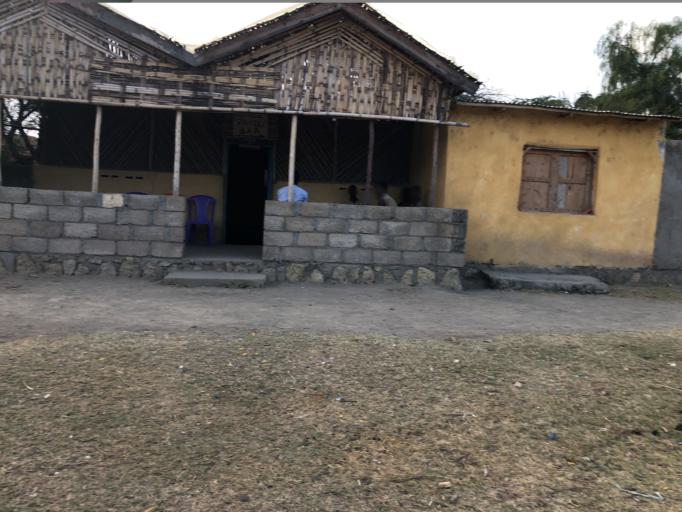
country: ET
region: Oromiya
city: Ziway
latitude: 7.5933
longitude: 38.6901
